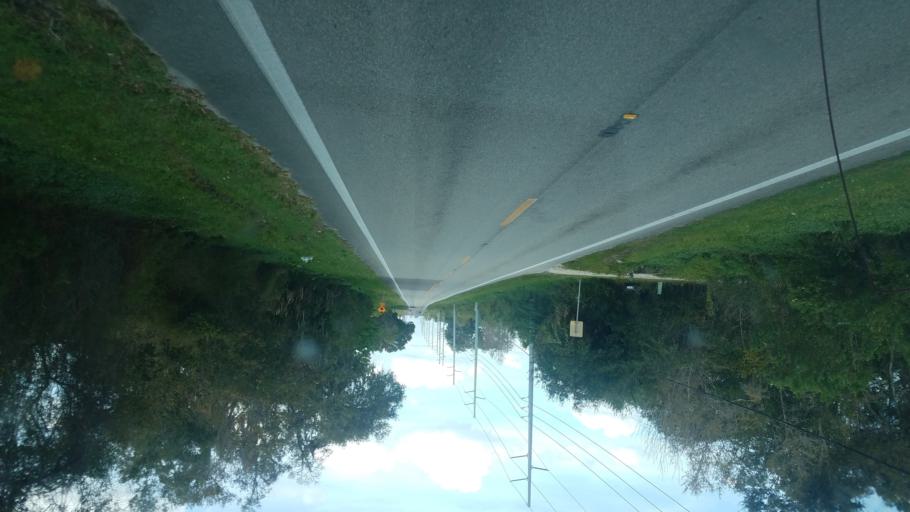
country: US
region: Florida
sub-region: Polk County
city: Haines City
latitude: 28.1141
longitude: -81.5939
